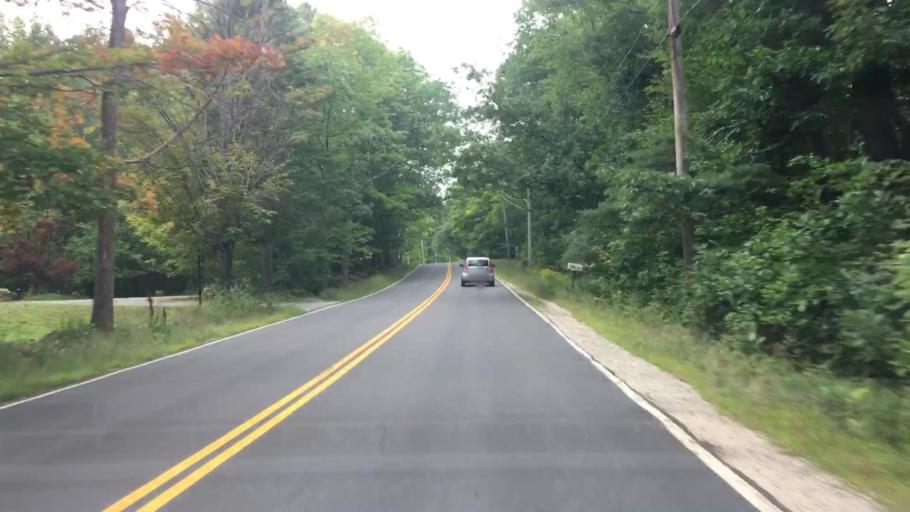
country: US
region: Maine
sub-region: Cumberland County
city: Cumberland Center
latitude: 43.8770
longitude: -70.2456
